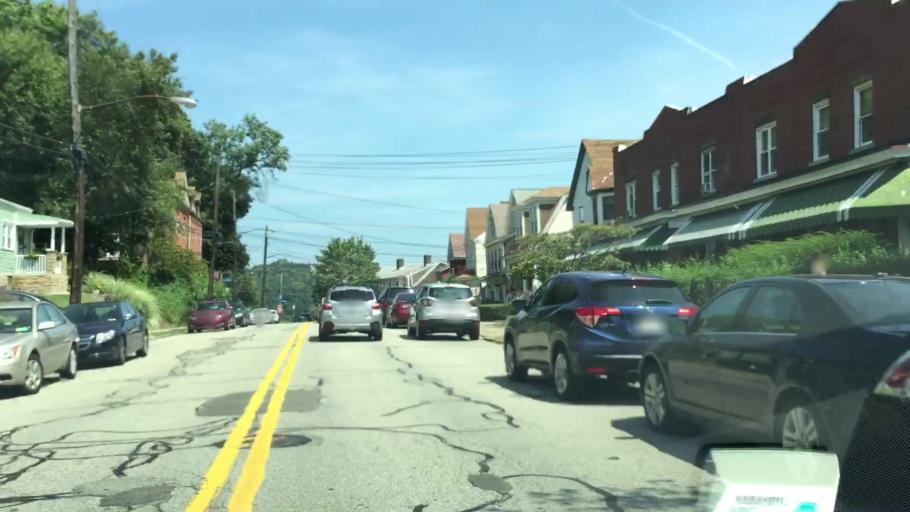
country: US
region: Pennsylvania
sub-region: Allegheny County
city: Sharpsburg
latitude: 40.4870
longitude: -79.9264
